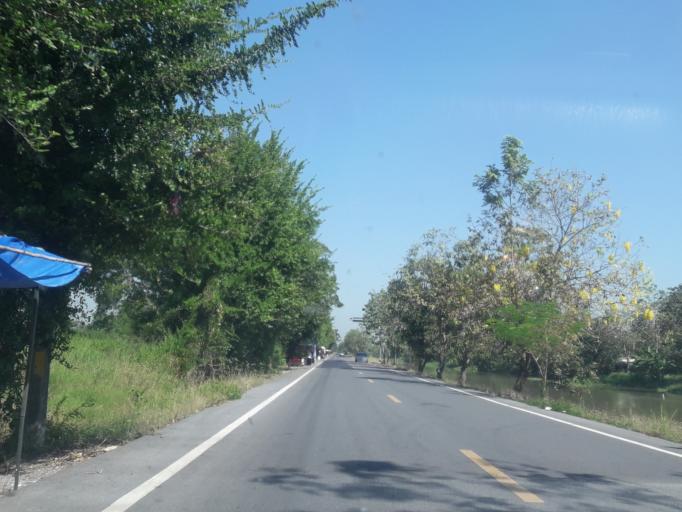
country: TH
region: Pathum Thani
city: Nong Suea
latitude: 14.1384
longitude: 100.8459
